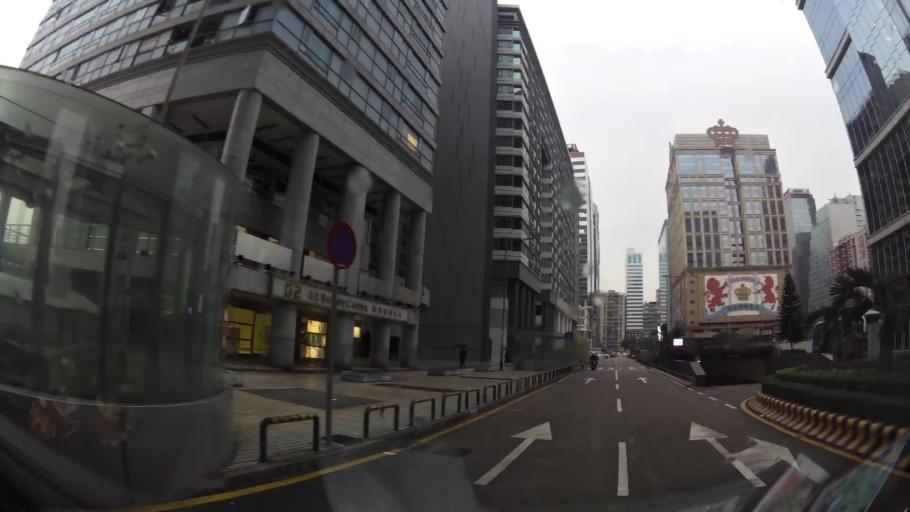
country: MO
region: Macau
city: Macau
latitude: 22.1892
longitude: 113.5418
